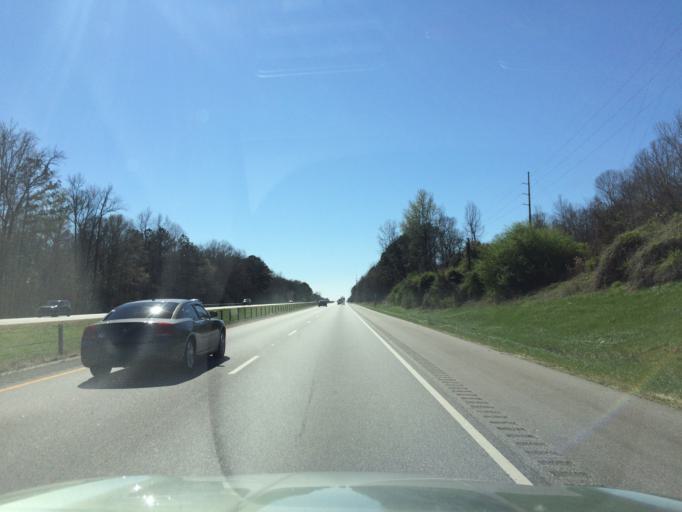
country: US
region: Alabama
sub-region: Lee County
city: Auburn
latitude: 32.5726
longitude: -85.4824
